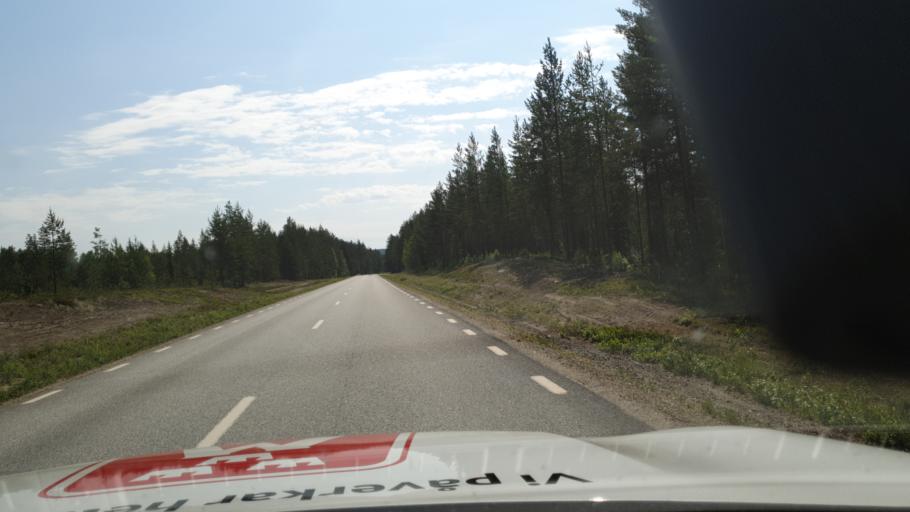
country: SE
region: Vaesterbotten
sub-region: Vindelns Kommun
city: Vindeln
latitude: 64.3738
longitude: 19.4123
